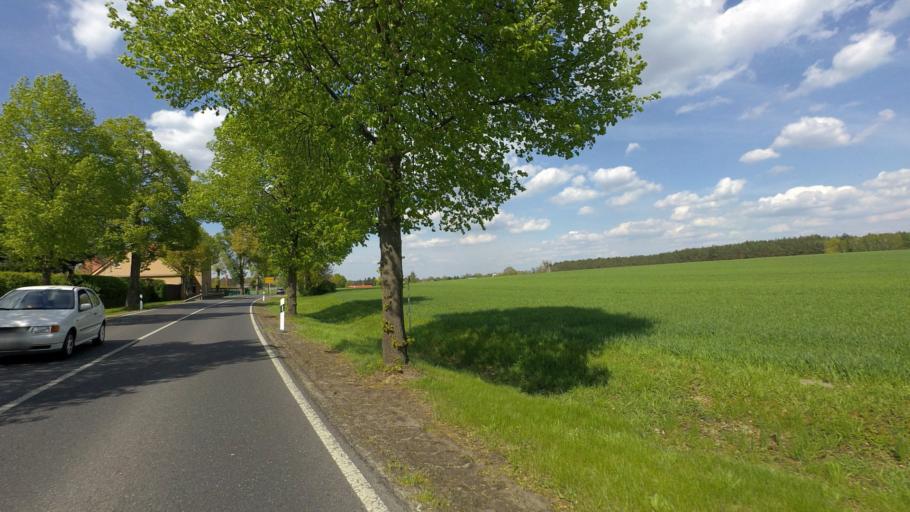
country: DE
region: Brandenburg
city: Marienwerder
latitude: 52.8947
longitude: 13.5384
